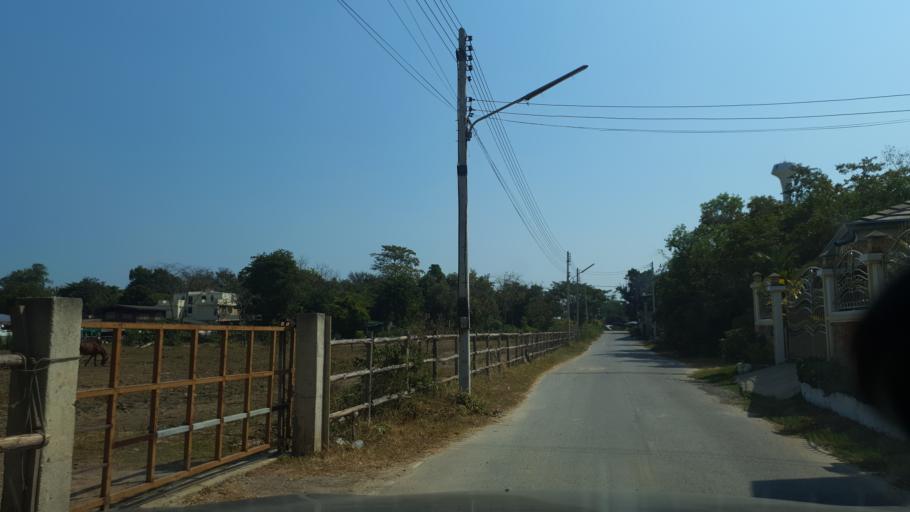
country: TH
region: Phetchaburi
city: Cha-am
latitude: 12.7836
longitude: 99.9762
